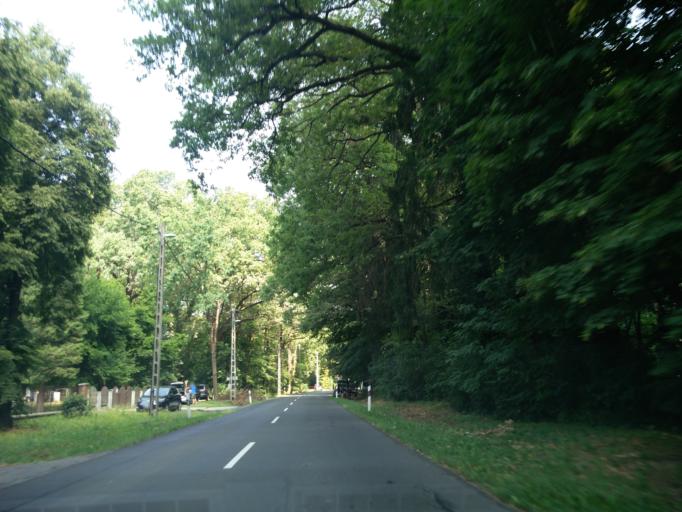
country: HU
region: Zala
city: Zalaegerszeg
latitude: 46.8132
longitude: 16.8233
